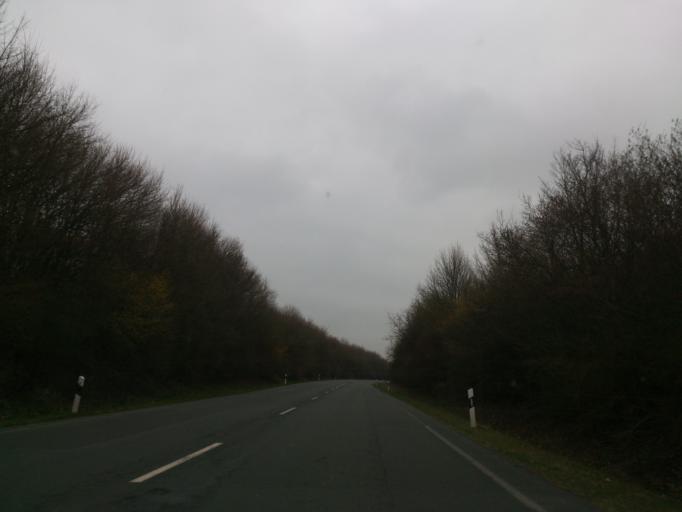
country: DE
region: North Rhine-Westphalia
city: Lichtenau
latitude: 51.5782
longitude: 8.8440
